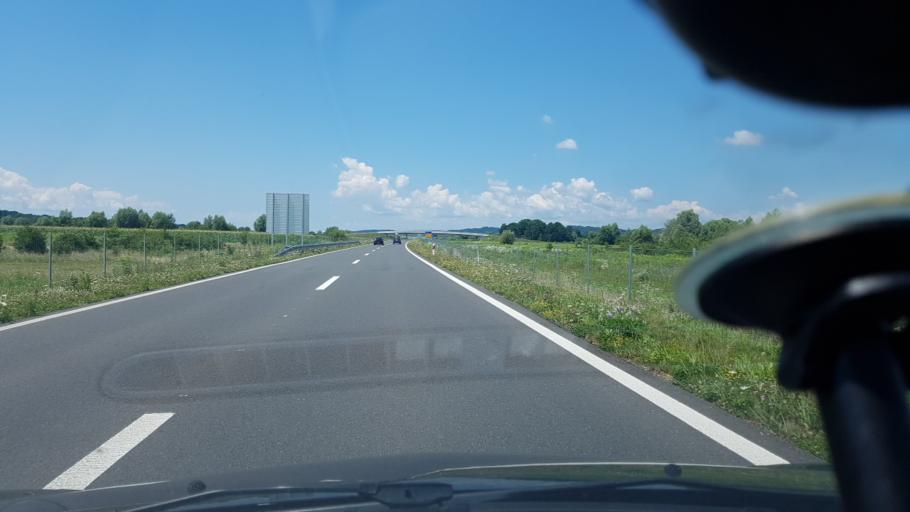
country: HR
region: Krapinsko-Zagorska
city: Bedekovcina
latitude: 46.0357
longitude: 16.0133
